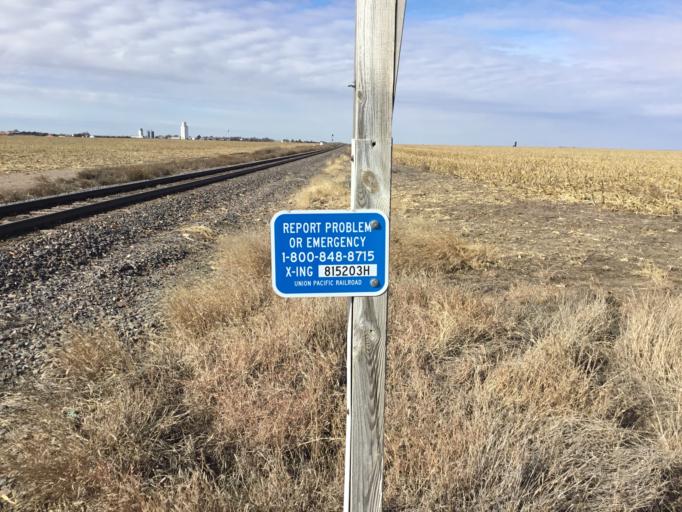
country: US
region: Kansas
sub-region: Trego County
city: WaKeeney
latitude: 39.0401
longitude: -100.0931
